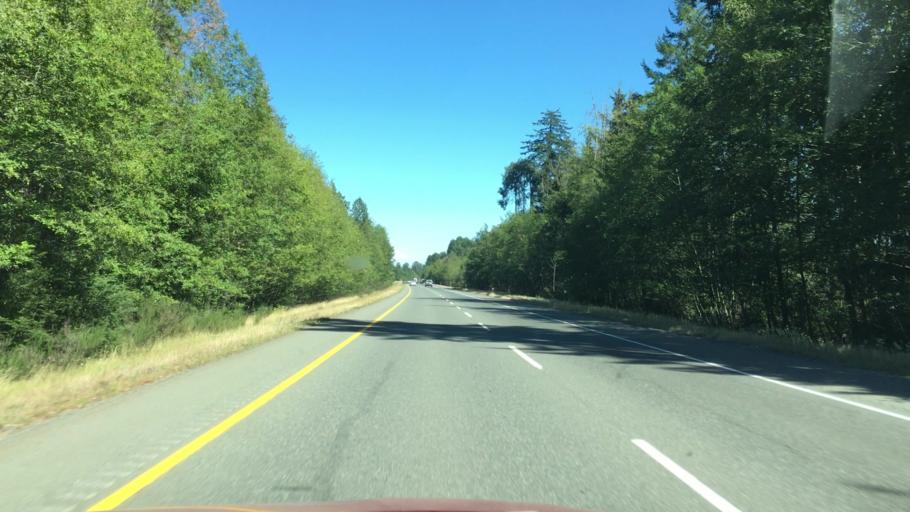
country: CA
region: British Columbia
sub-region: Regional District of Nanaimo
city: Parksville
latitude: 49.3169
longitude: -124.3825
